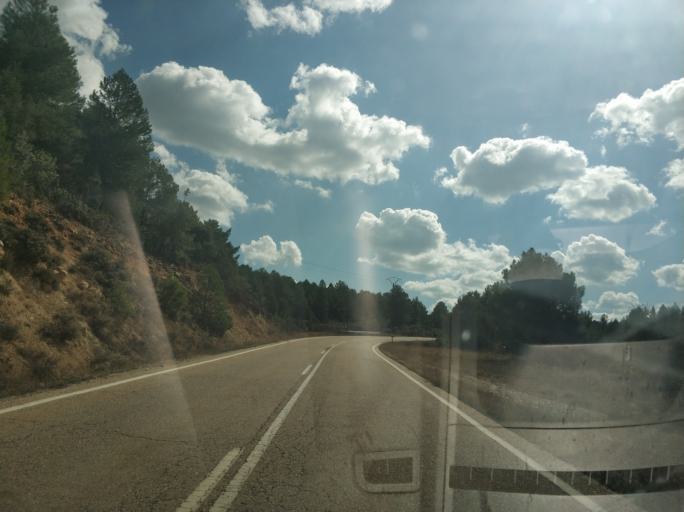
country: ES
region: Castille and Leon
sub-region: Provincia de Soria
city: Casarejos
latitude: 41.7800
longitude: -3.0275
